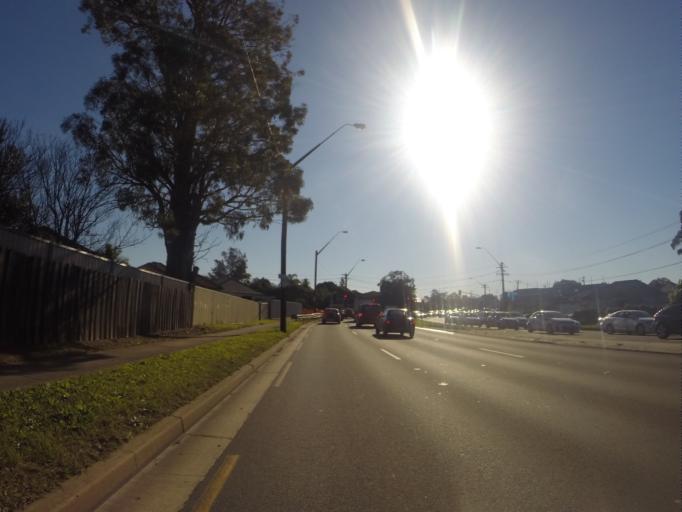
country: AU
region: New South Wales
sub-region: Canterbury
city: Lakemba
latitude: -33.9164
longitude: 151.0635
